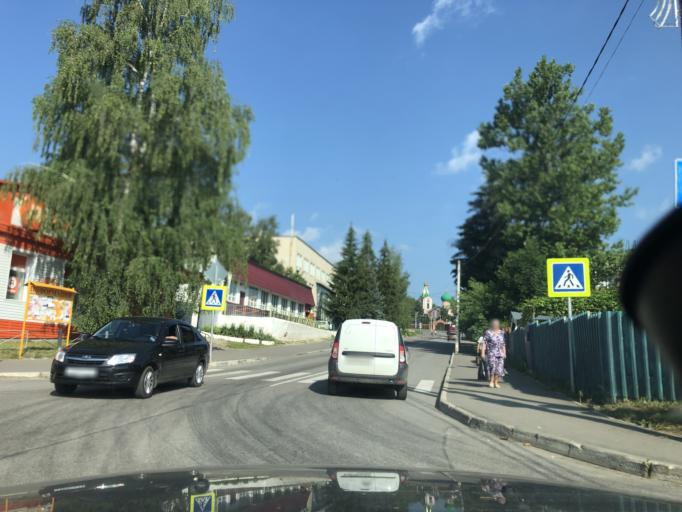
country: RU
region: Tula
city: Dubna
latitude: 54.1513
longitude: 36.9632
